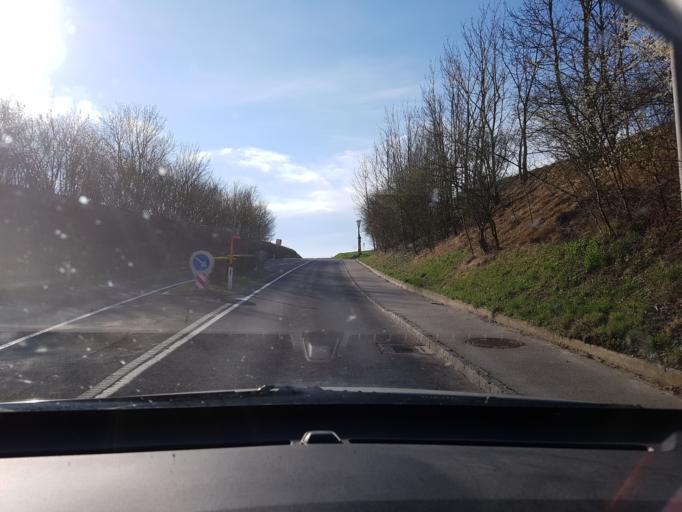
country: AT
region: Upper Austria
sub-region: Politischer Bezirk Linz-Land
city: Asten
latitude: 48.2056
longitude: 14.4223
